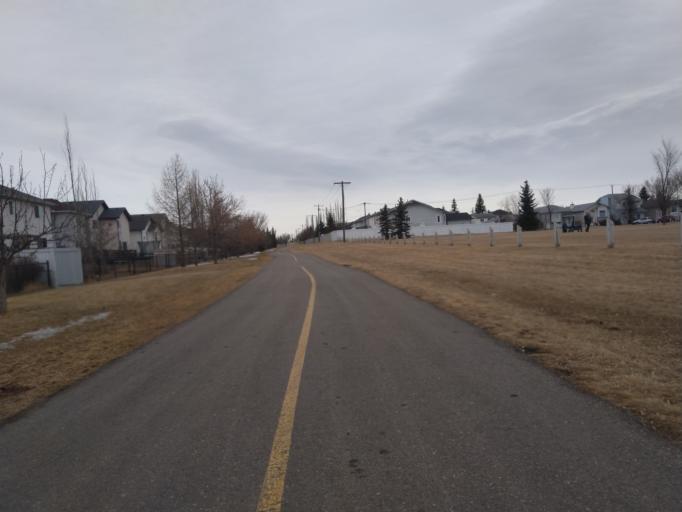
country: CA
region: Alberta
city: Calgary
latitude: 51.1587
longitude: -114.0481
